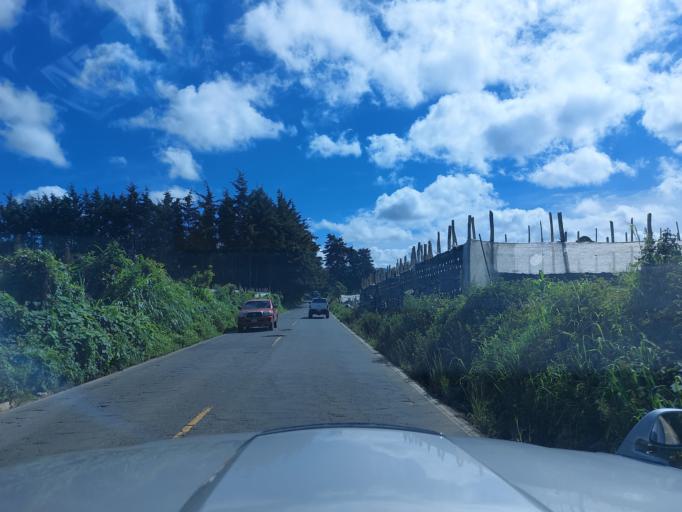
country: GT
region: Chimaltenango
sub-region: Municipio de Zaragoza
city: Zaragoza
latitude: 14.6691
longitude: -90.9003
